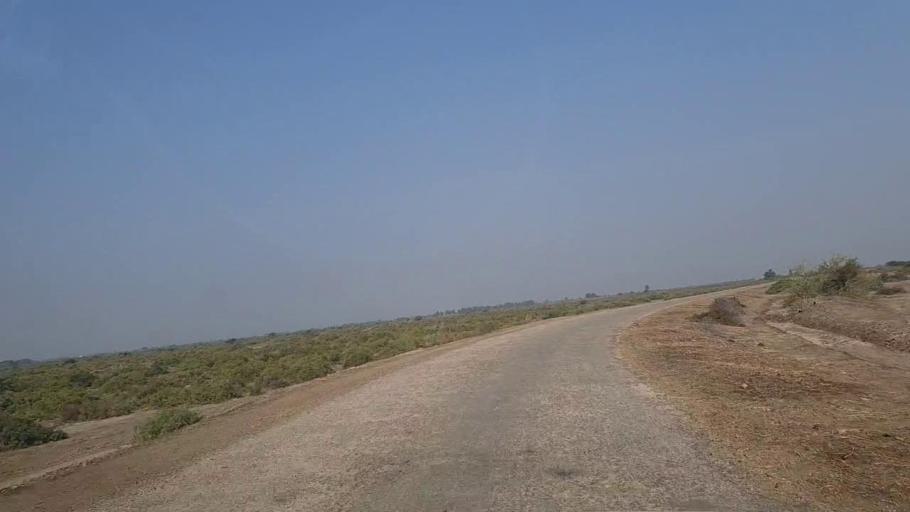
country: PK
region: Sindh
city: Keti Bandar
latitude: 24.2439
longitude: 67.6934
